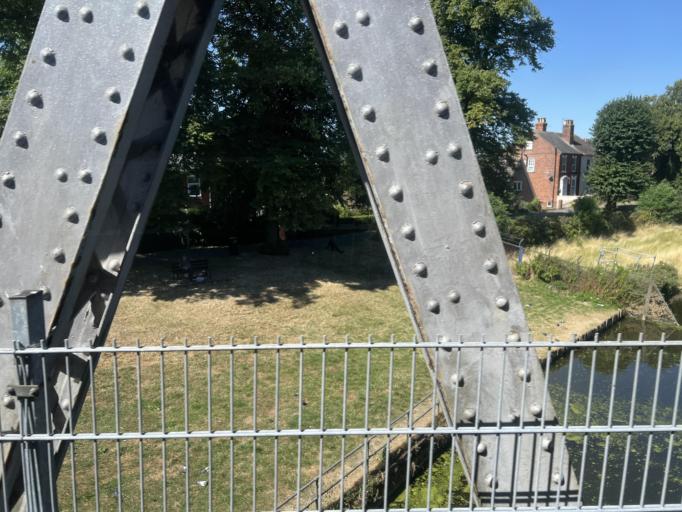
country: GB
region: England
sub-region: Lincolnshire
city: Boston
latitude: 52.9816
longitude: -0.0303
